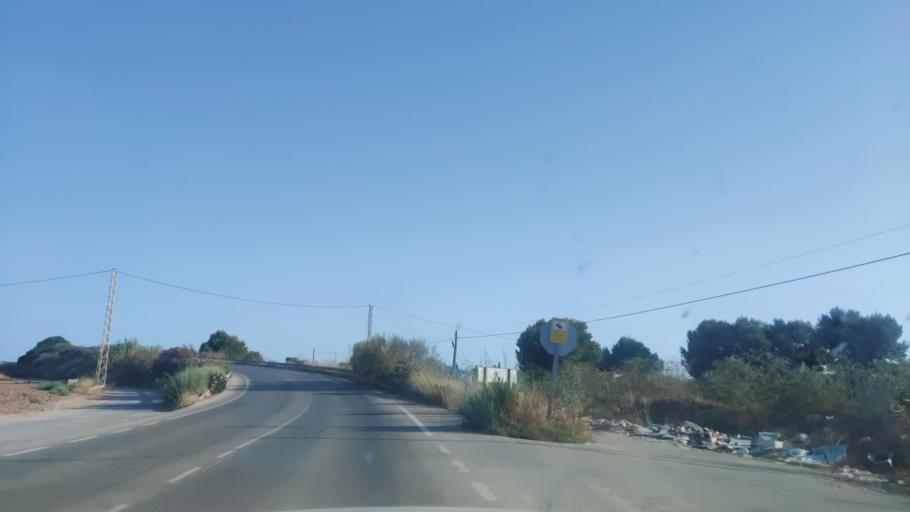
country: ES
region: Murcia
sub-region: Murcia
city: Los Alcazares
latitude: 37.7526
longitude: -0.8569
